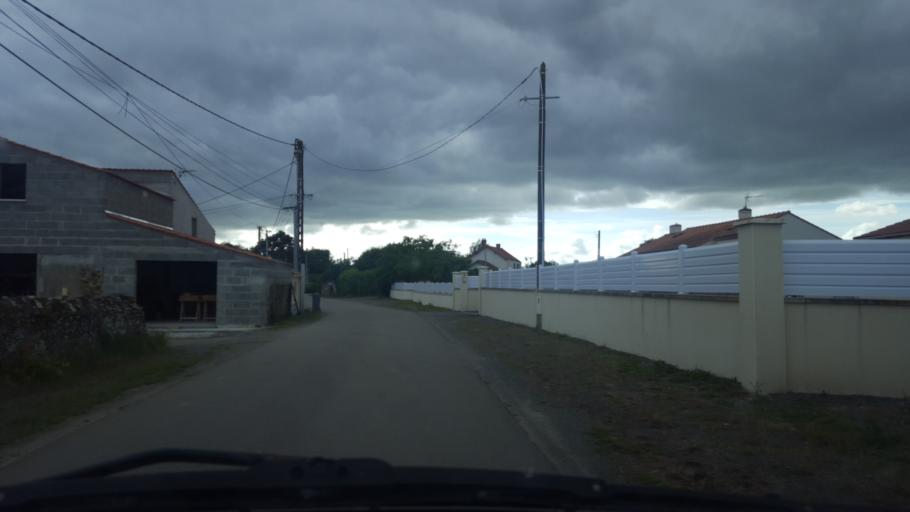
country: FR
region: Pays de la Loire
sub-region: Departement de la Loire-Atlantique
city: Saint-Philbert-de-Grand-Lieu
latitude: 47.0146
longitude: -1.6733
